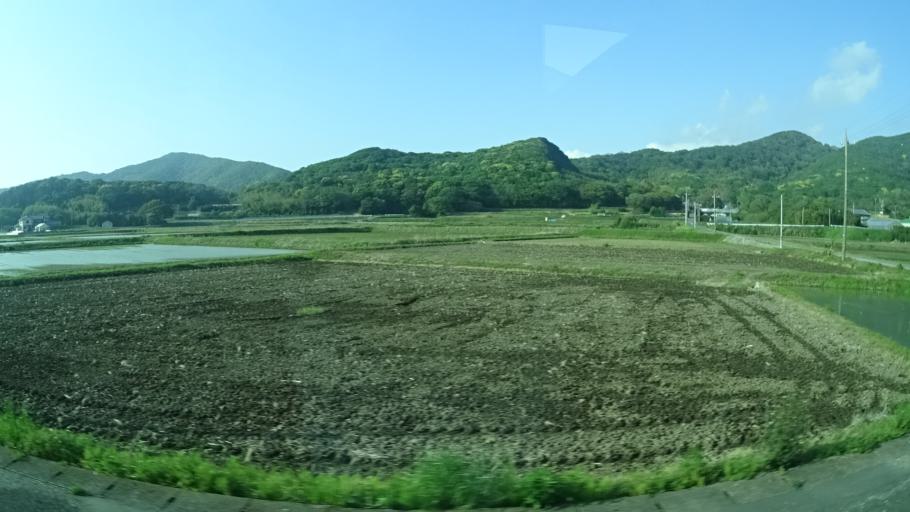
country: JP
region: Aichi
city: Tahara
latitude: 34.6537
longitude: 137.2137
